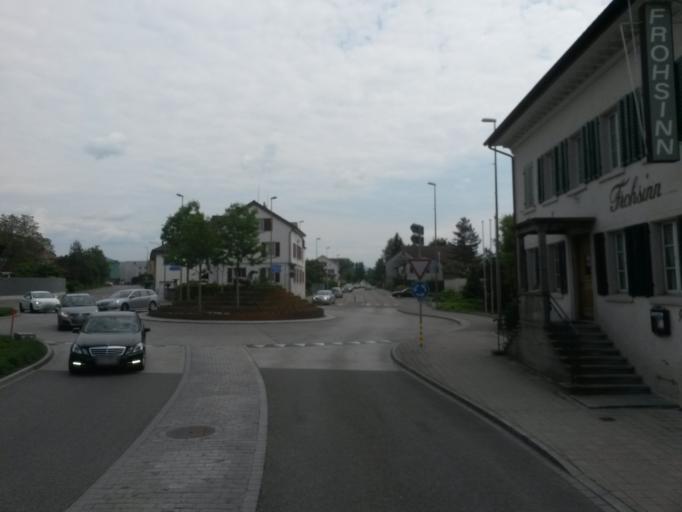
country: CH
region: Zurich
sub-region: Bezirk Pfaeffikon
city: Fehraltorf
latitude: 47.3864
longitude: 8.7546
